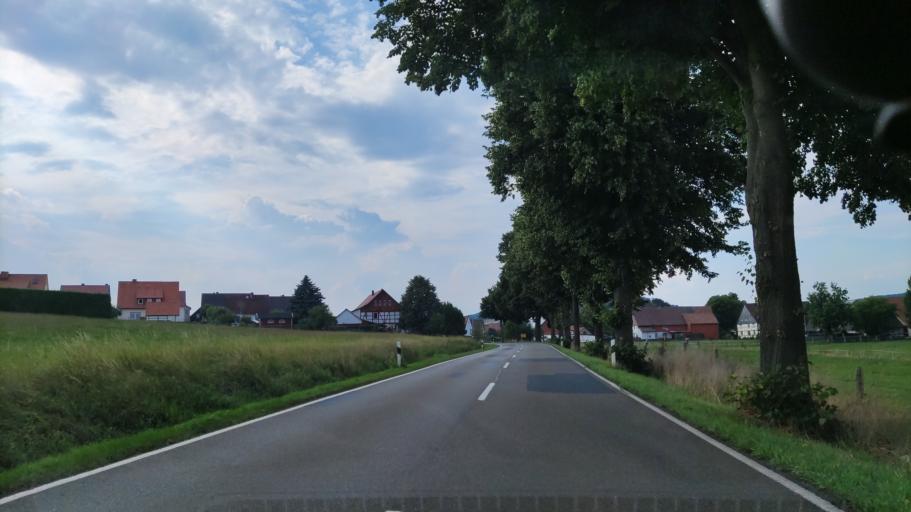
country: DE
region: Lower Saxony
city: Eimen
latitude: 51.8309
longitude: 9.8011
